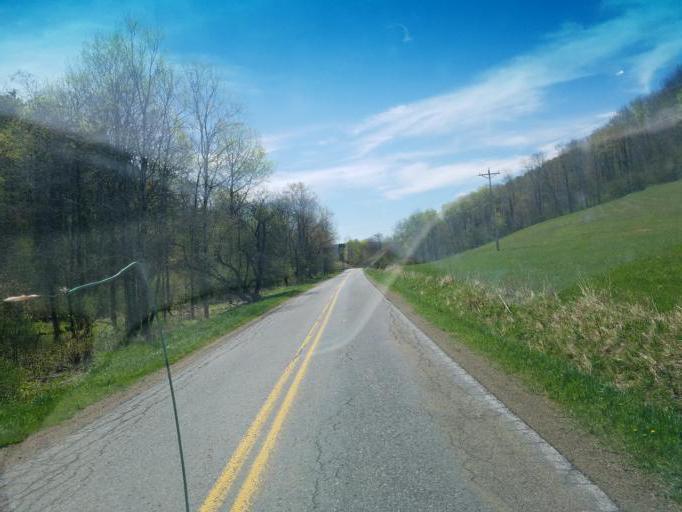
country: US
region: Pennsylvania
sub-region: Potter County
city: Galeton
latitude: 41.8758
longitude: -77.7288
